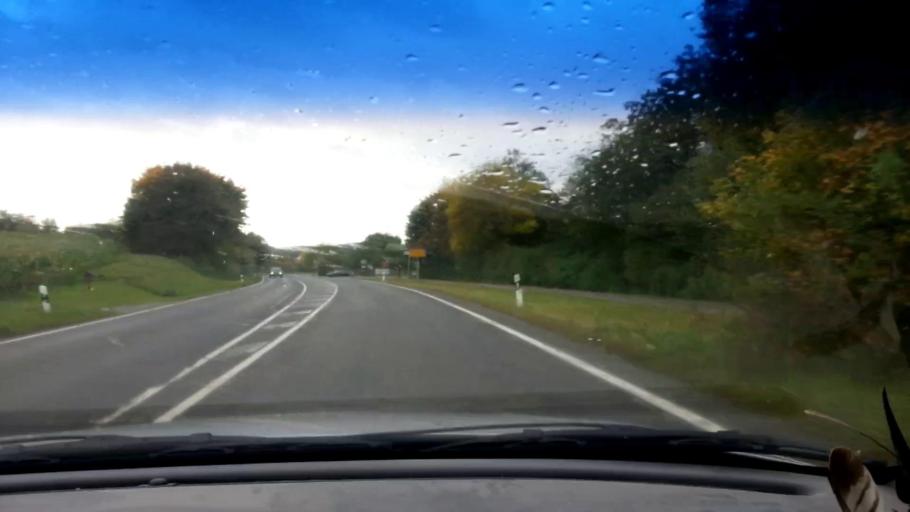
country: DE
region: Bavaria
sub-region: Upper Franconia
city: Stegaurach
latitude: 49.8647
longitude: 10.8562
